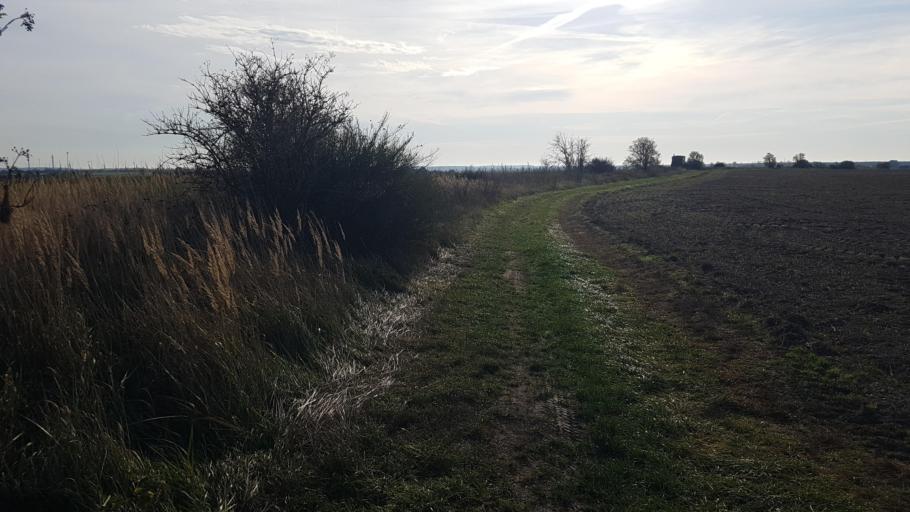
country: DE
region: Brandenburg
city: Ihlow
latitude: 51.8812
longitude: 13.3703
